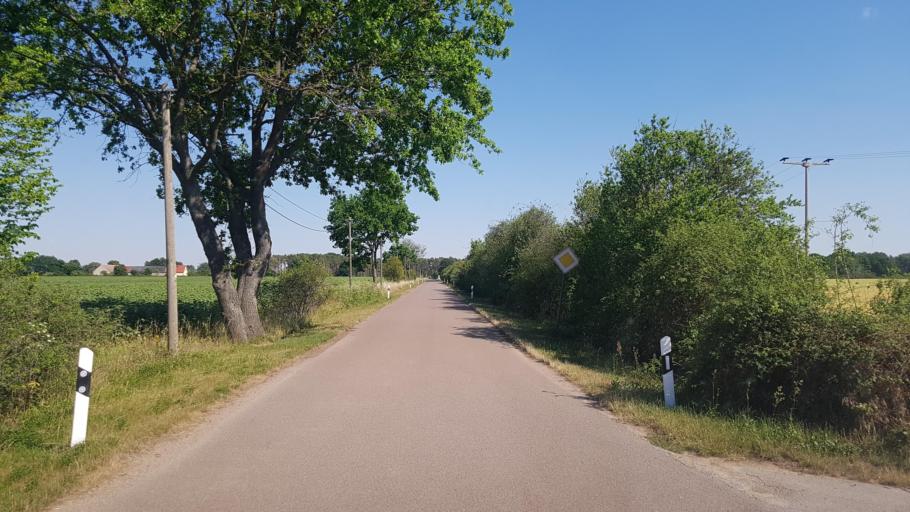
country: DE
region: Saxony-Anhalt
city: Elster
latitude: 51.7648
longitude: 12.8736
